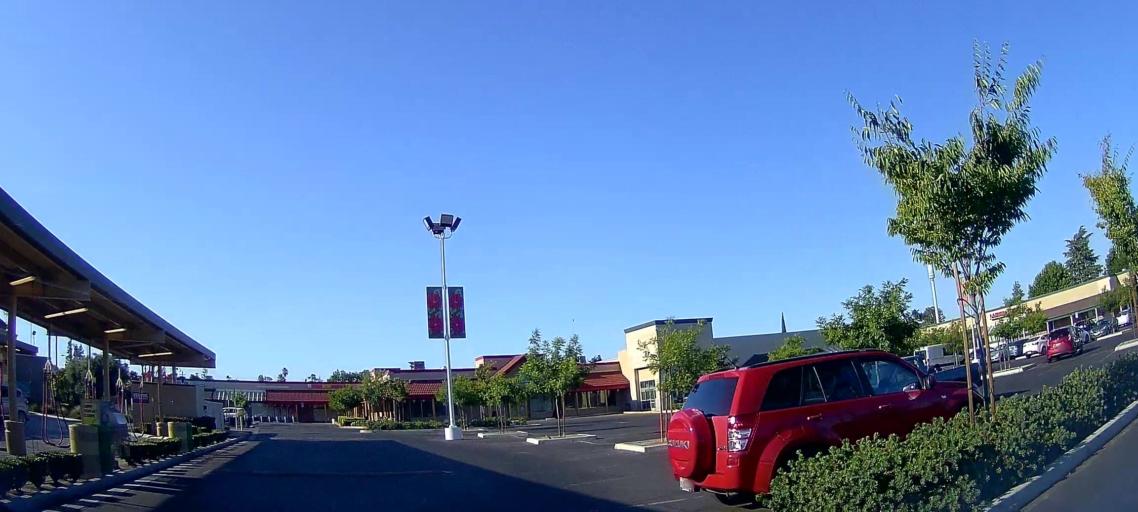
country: US
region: California
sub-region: Fresno County
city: Fresno
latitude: 36.8231
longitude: -119.8077
